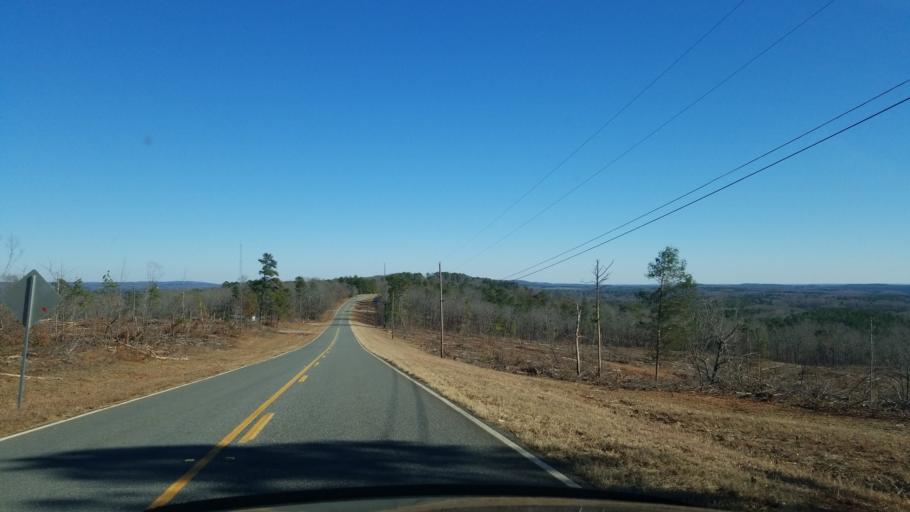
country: US
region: Georgia
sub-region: Meriwether County
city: Manchester
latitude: 32.8423
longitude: -84.6717
